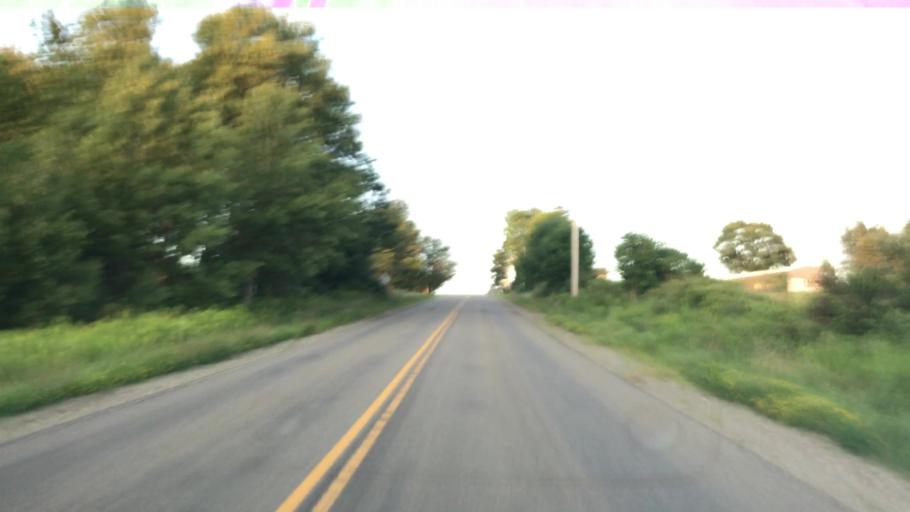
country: US
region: New York
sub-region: Chautauqua County
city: Mayville
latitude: 42.2855
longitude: -79.4331
